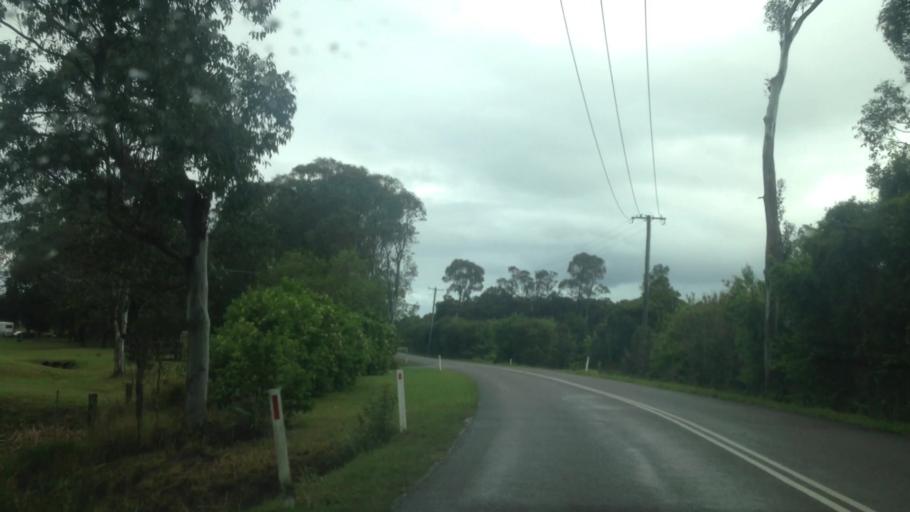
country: AU
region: New South Wales
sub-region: Wyong Shire
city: Little Jilliby
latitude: -33.2522
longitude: 151.3831
